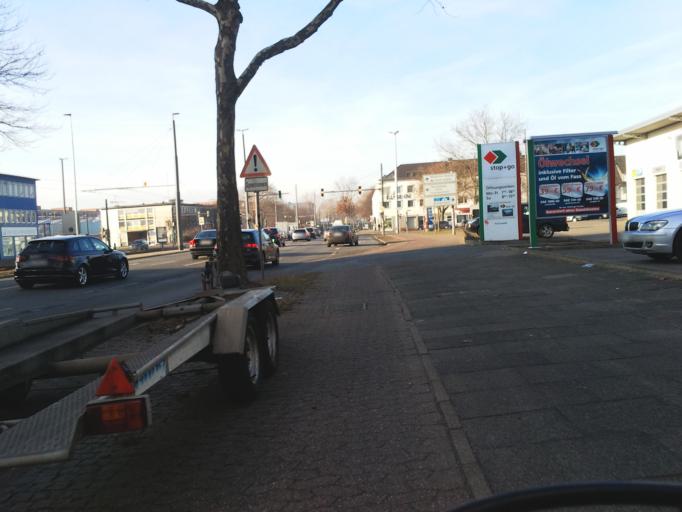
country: DE
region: Bremen
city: Bremen
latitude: 53.0880
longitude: 8.7867
